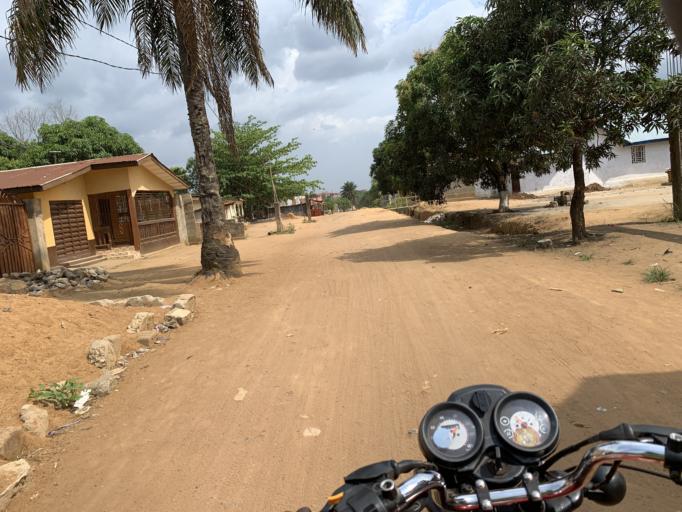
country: SL
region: Western Area
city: Waterloo
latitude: 8.3382
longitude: -13.0528
